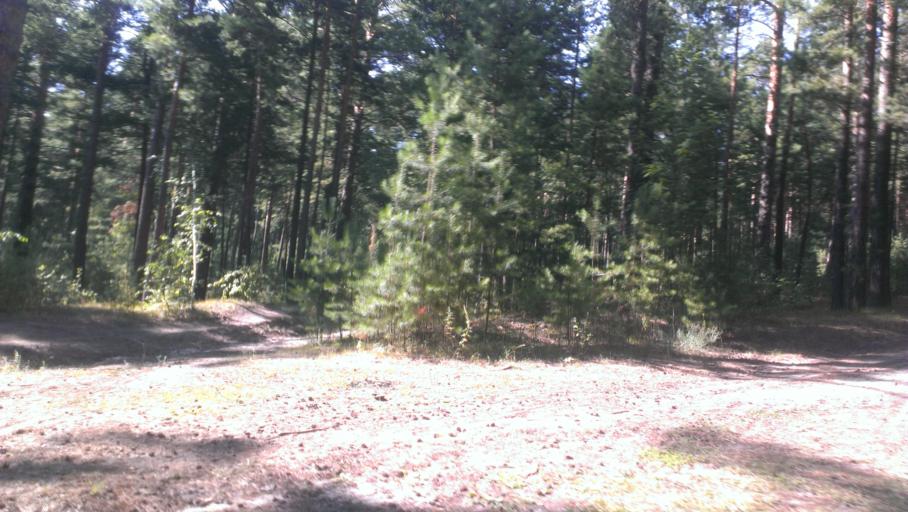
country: RU
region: Altai Krai
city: Novosilikatnyy
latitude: 53.3157
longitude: 83.6848
